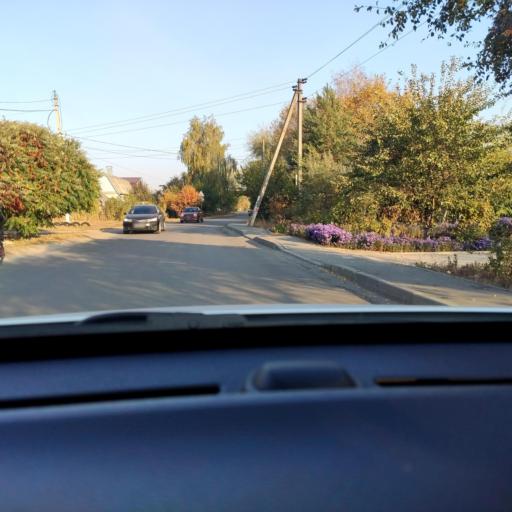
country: RU
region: Voronezj
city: Somovo
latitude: 51.6851
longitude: 39.3210
